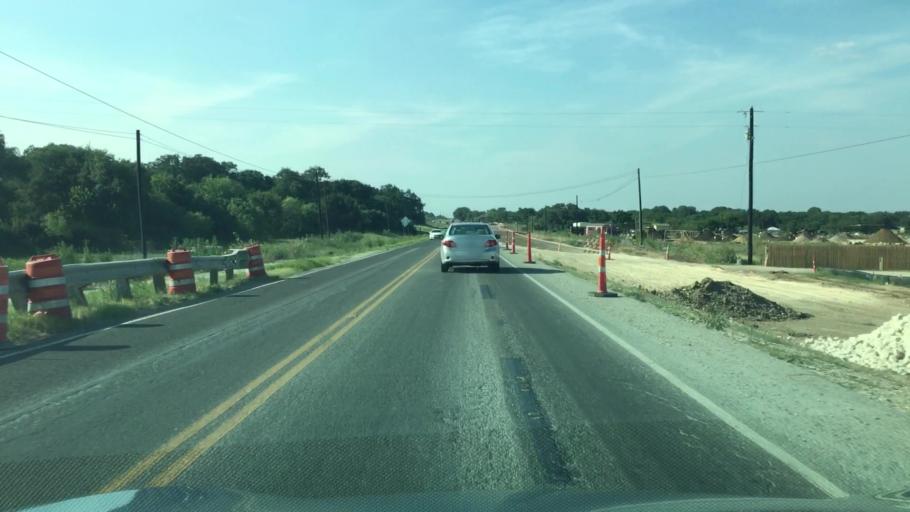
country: US
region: Texas
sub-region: Hays County
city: Buda
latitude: 30.0706
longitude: -97.8742
